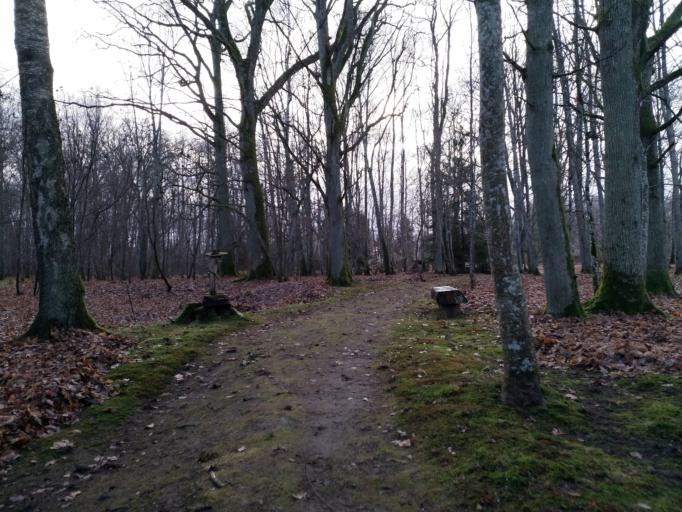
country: LV
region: Aizpute
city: Aizpute
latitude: 56.8315
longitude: 21.7739
